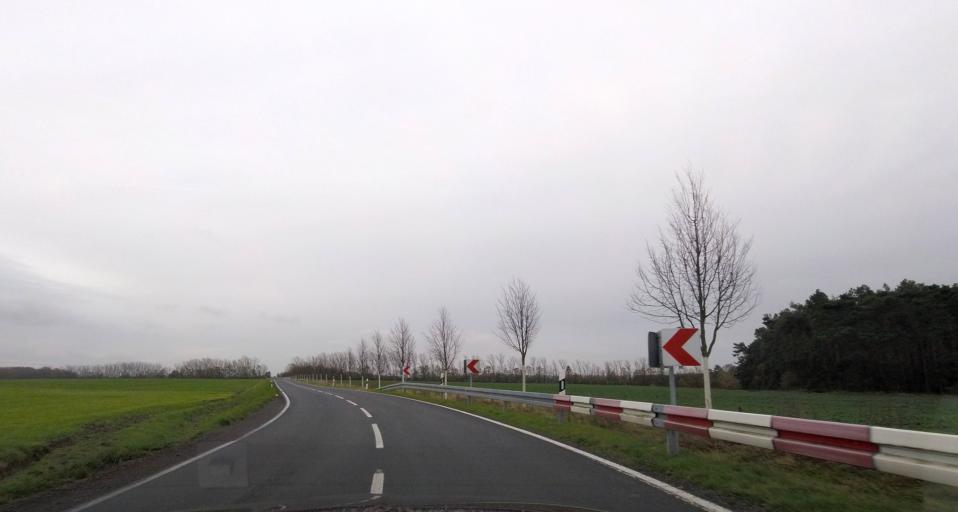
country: DE
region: Brandenburg
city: Niemegk
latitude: 52.0383
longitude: 12.7170
